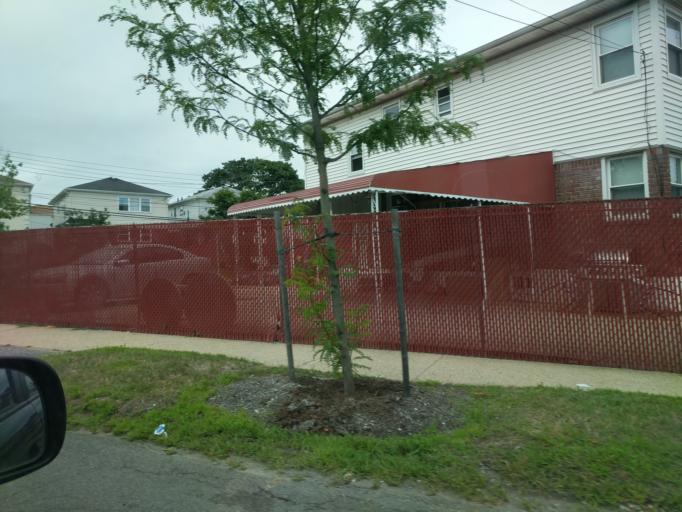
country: US
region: New York
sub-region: Nassau County
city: South Valley Stream
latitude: 40.6566
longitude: -73.7278
